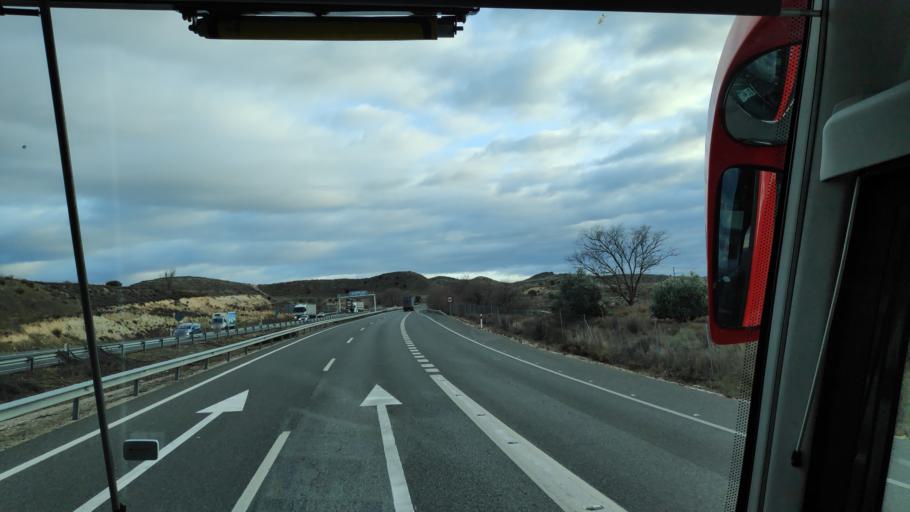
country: ES
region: Madrid
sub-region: Provincia de Madrid
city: Perales de Tajuna
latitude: 40.2216
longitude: -3.3307
